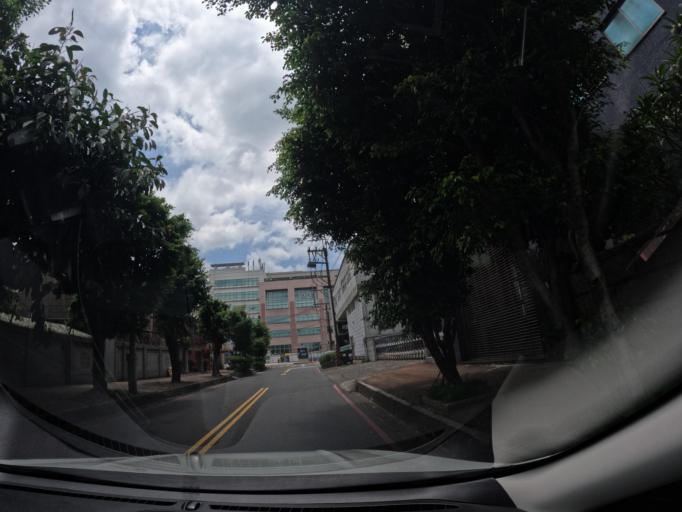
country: TW
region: Taipei
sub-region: Taipei
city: Banqiao
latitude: 24.9653
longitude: 121.4241
